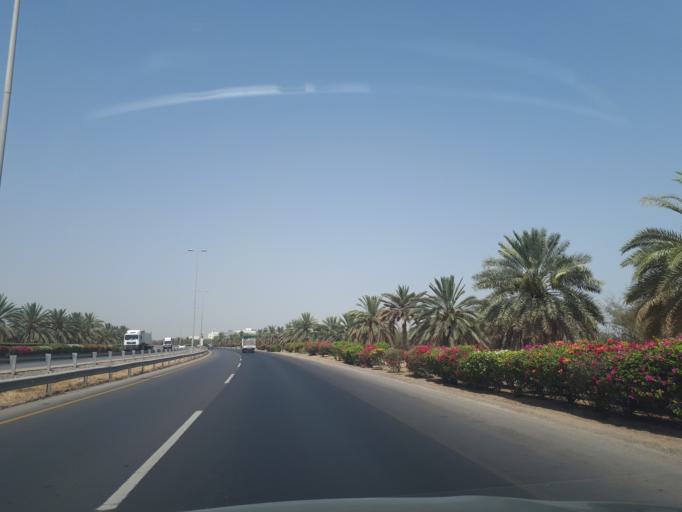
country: OM
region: Muhafazat Masqat
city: As Sib al Jadidah
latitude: 23.5919
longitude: 58.2080
